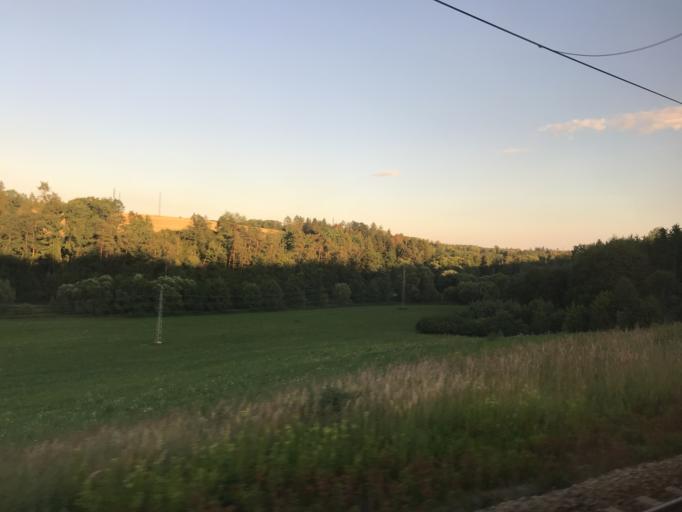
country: CZ
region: Central Bohemia
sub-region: Okres Benesov
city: Benesov
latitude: 49.8057
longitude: 14.7087
